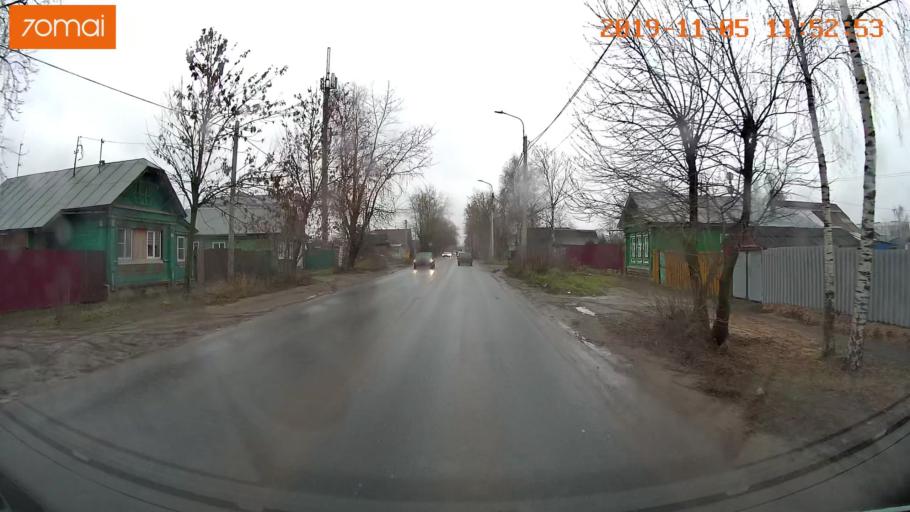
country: RU
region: Ivanovo
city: Bogorodskoye
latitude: 56.9977
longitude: 41.0299
